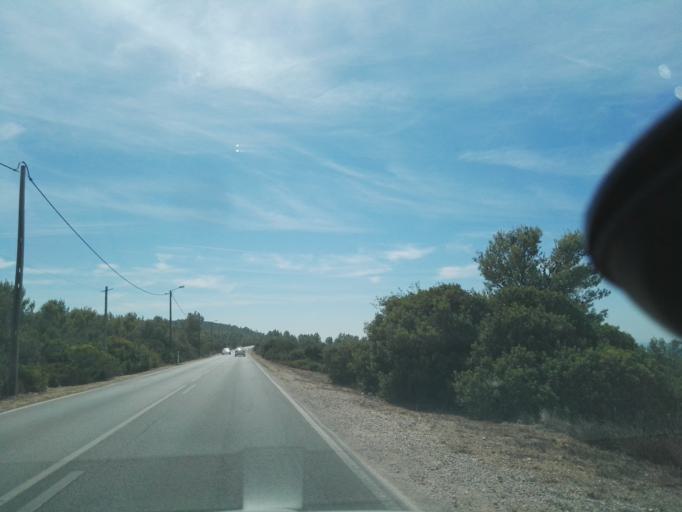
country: PT
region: Setubal
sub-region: Sesimbra
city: Sesimbra
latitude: 38.4550
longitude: -9.0923
